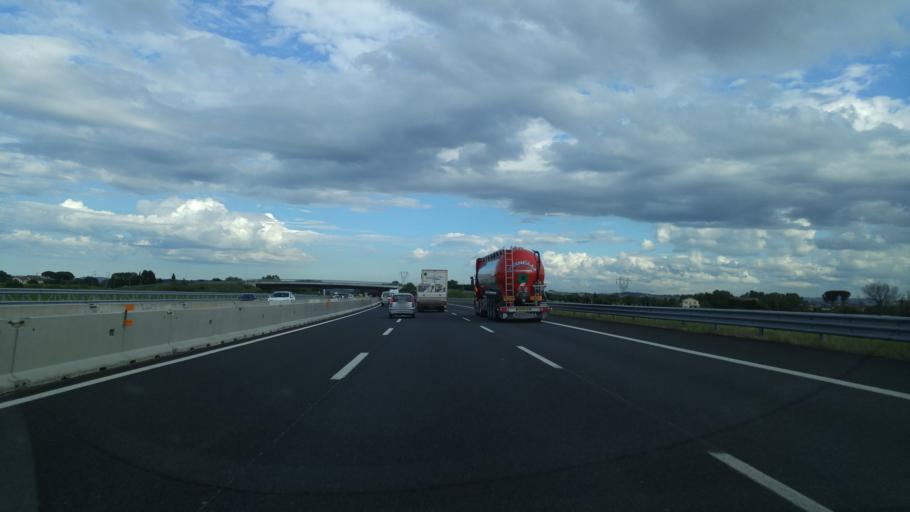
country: IT
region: Emilia-Romagna
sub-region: Provincia di Rimini
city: Coriano
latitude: 44.0017
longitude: 12.6050
